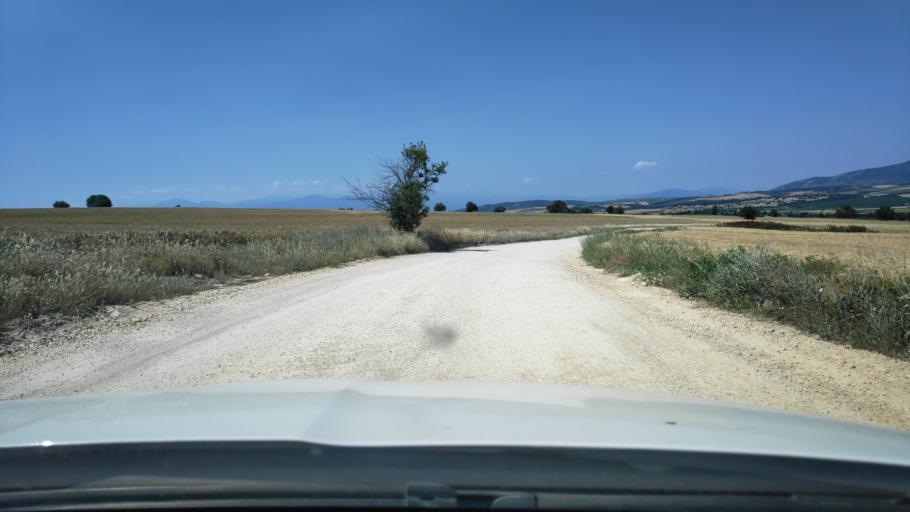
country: MK
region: Kumanovo
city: Romanovce
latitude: 42.0772
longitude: 21.7187
